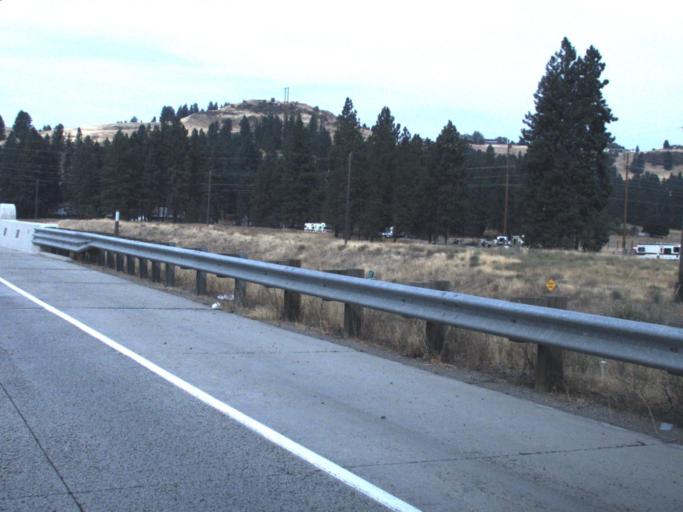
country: US
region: Washington
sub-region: Spokane County
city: Mead
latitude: 47.7186
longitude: -117.3578
